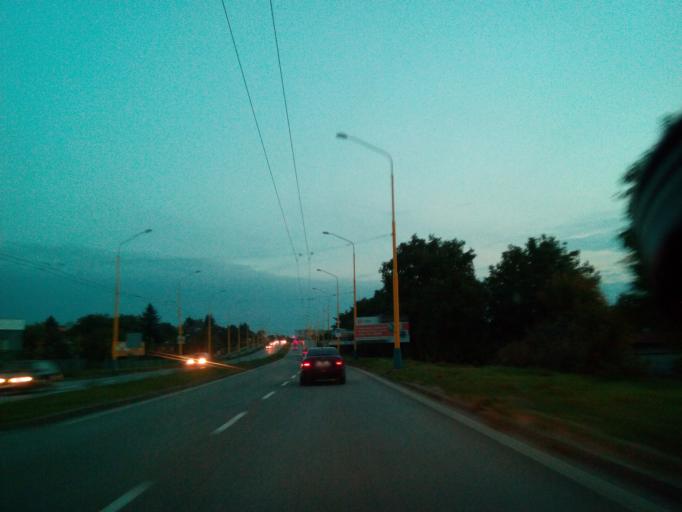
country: SK
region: Presovsky
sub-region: Okres Presov
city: Presov
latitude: 48.9827
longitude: 21.2635
